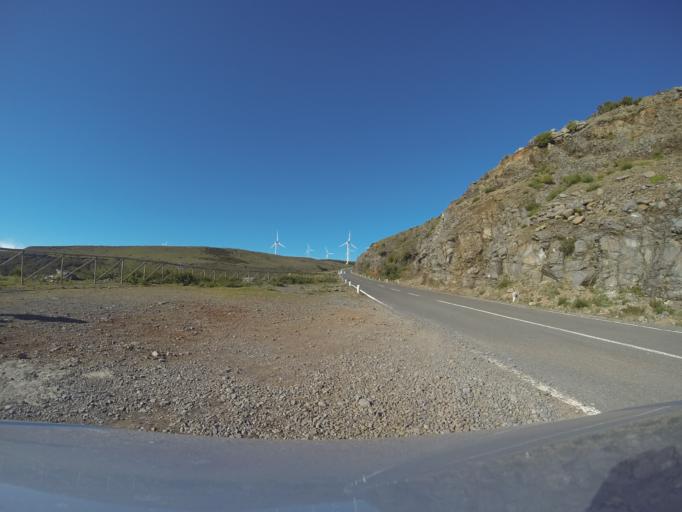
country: PT
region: Madeira
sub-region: Sao Vicente
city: Sao Vicente
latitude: 32.7369
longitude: -17.0613
